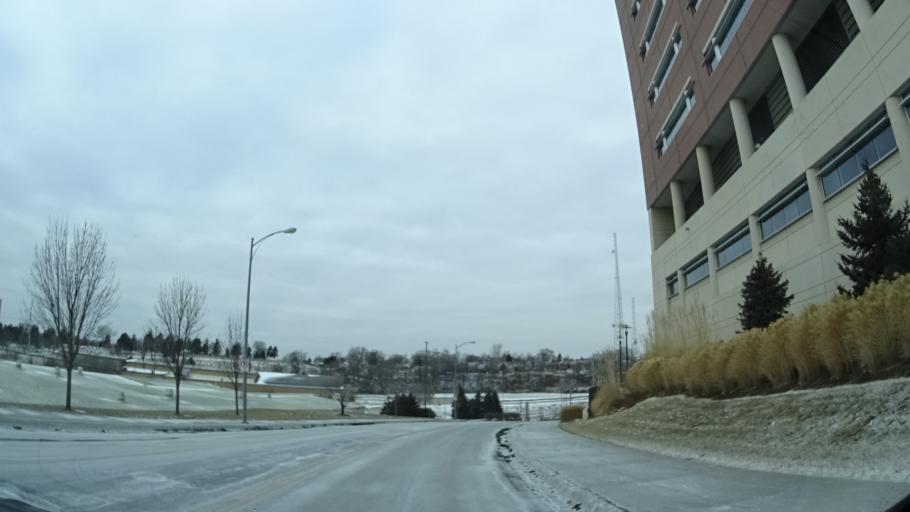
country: US
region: Nebraska
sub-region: Douglas County
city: Omaha
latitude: 41.2544
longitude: -95.9812
